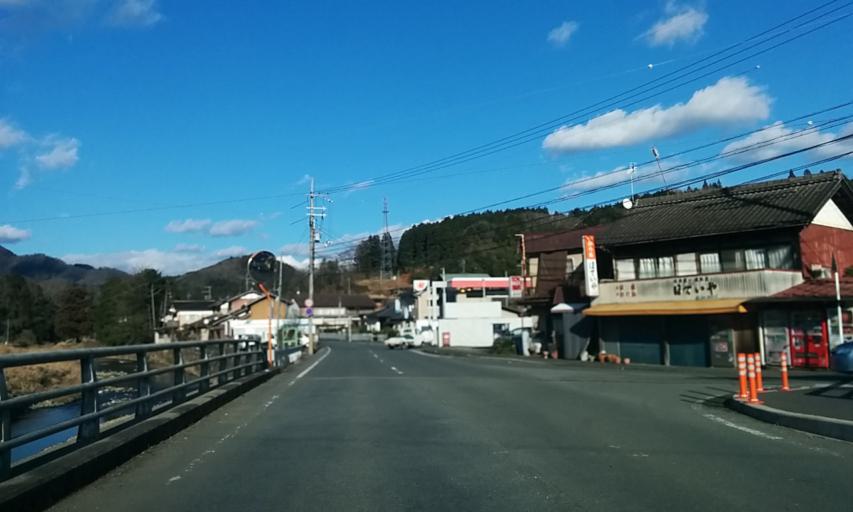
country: JP
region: Kyoto
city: Fukuchiyama
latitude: 35.2867
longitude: 135.0678
